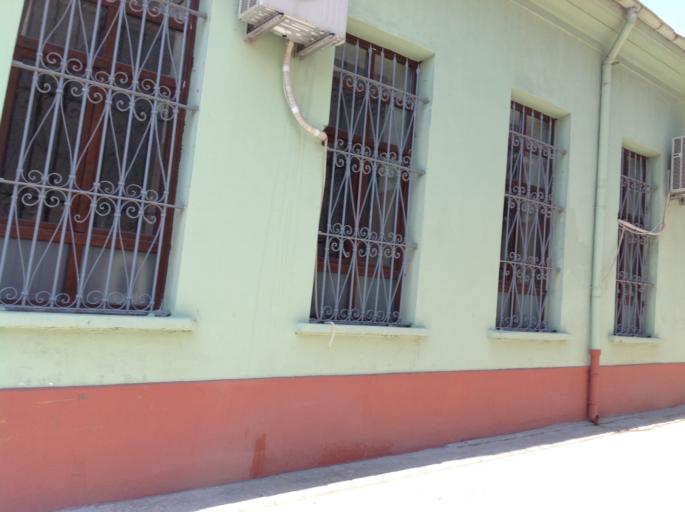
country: TR
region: Istanbul
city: Eminoenue
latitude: 41.0032
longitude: 28.9796
